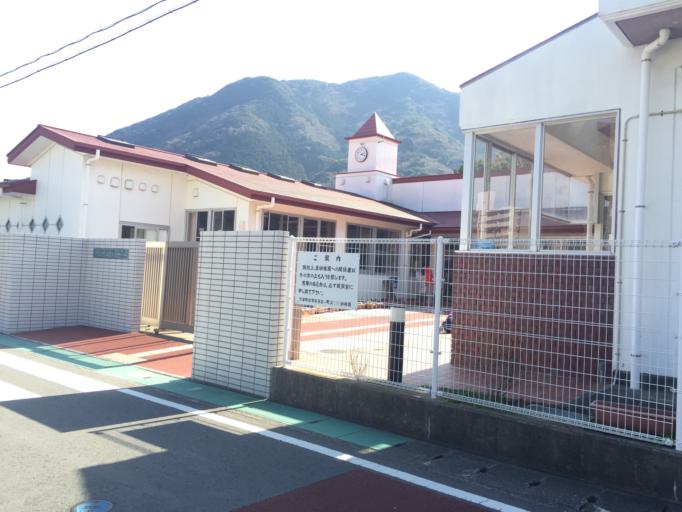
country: JP
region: Shizuoka
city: Shimoda
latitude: 34.7479
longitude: 138.9939
